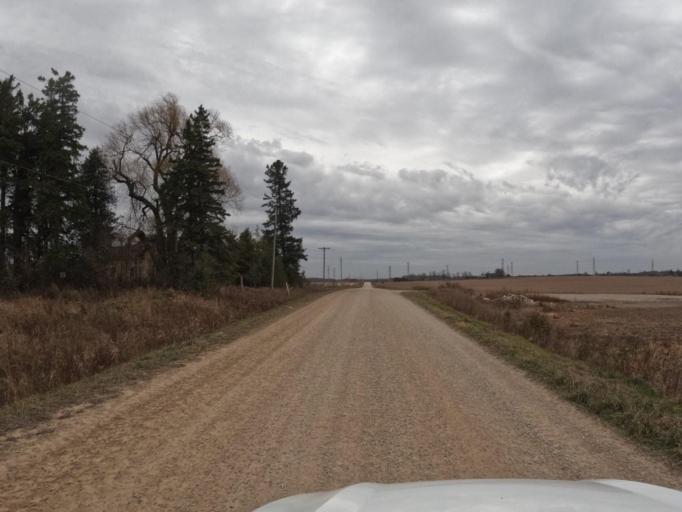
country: CA
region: Ontario
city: Shelburne
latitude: 44.0020
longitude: -80.3874
